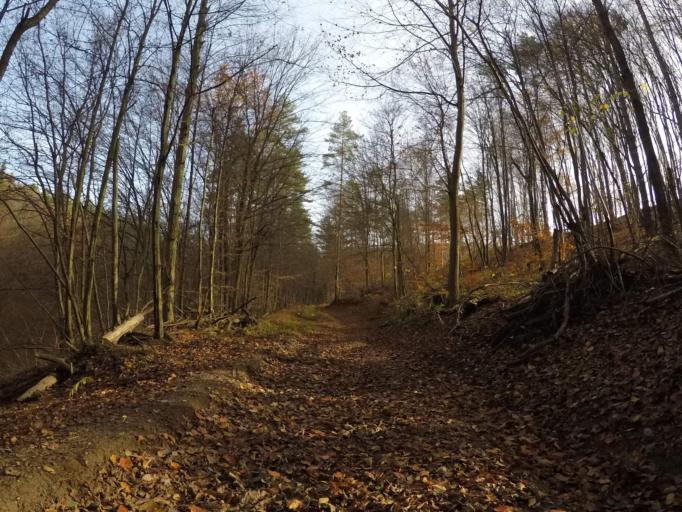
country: SK
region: Presovsky
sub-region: Okres Presov
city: Presov
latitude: 48.9177
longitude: 21.2101
